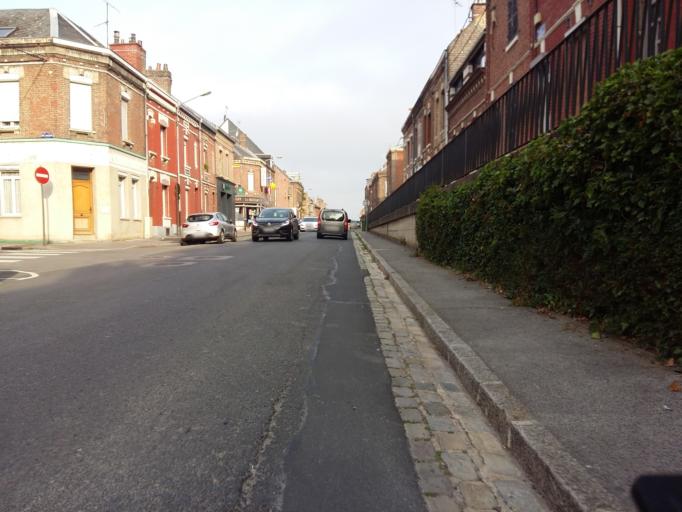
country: FR
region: Picardie
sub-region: Departement de la Somme
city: Rivery
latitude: 49.9034
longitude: 2.3141
